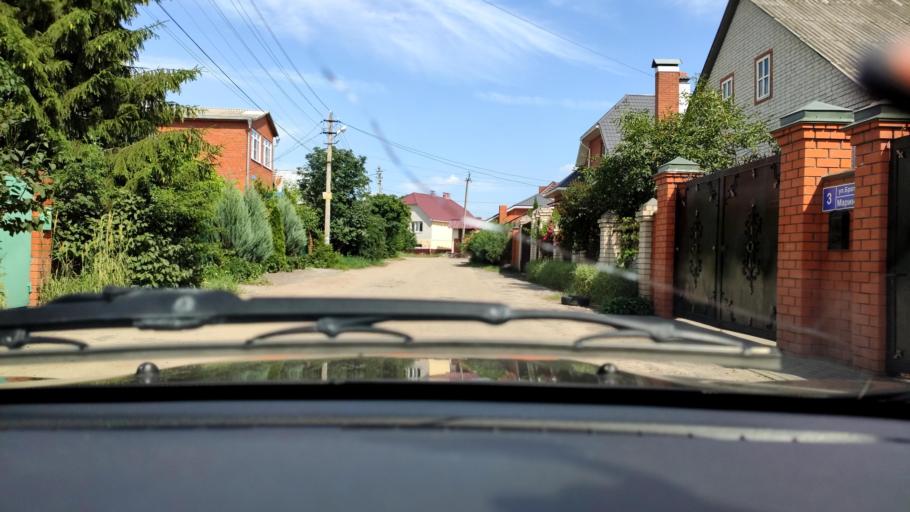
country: RU
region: Voronezj
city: Podgornoye
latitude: 51.7434
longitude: 39.1569
